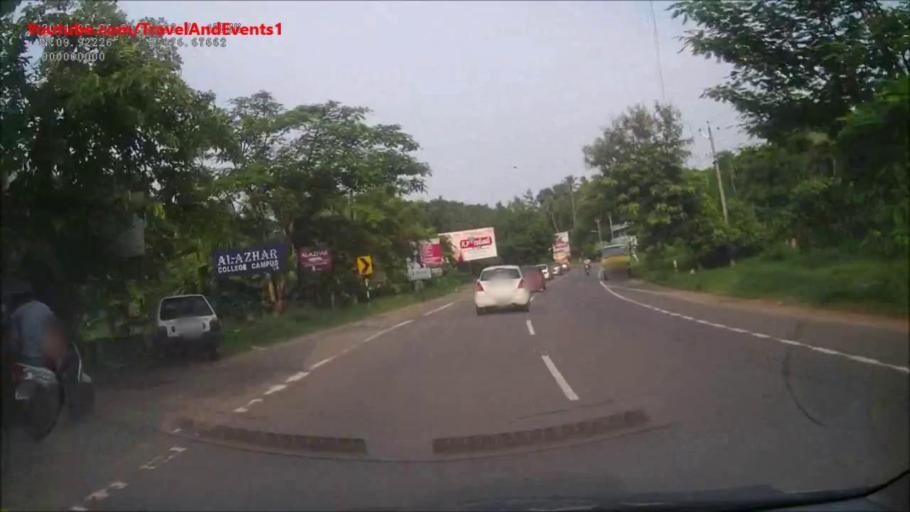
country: IN
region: Kerala
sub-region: Ernakulam
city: Muvattupula
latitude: 9.9221
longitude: 76.6767
